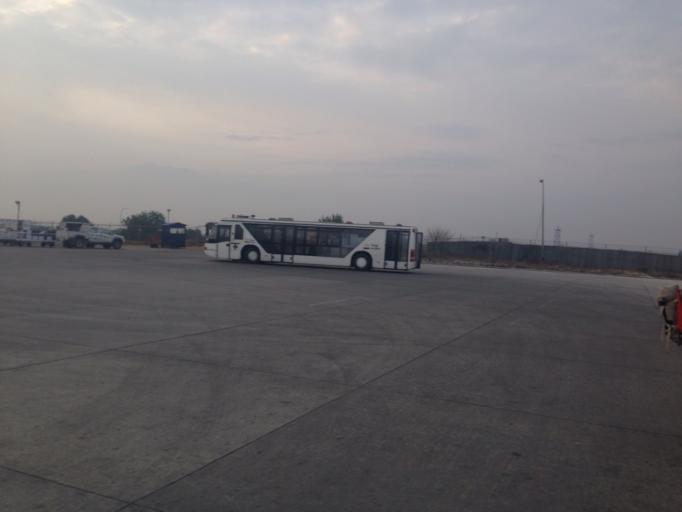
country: NP
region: Central Region
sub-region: Bagmati Zone
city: Kathmandu
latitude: 27.6983
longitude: 85.3570
